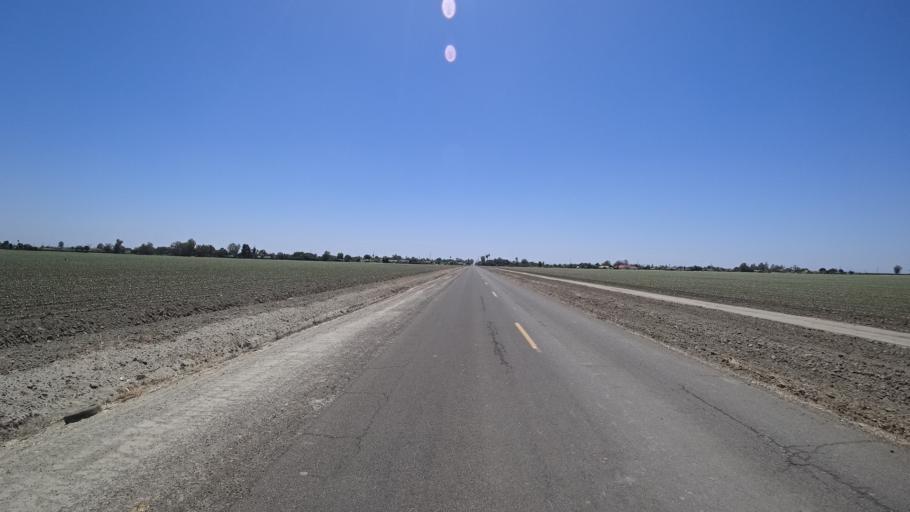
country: US
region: California
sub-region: Kings County
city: Corcoran
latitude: 36.1140
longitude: -119.5812
